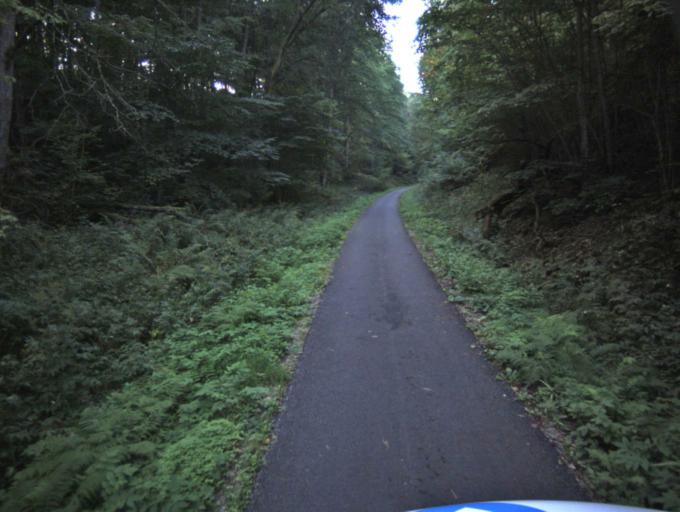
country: SE
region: Vaestra Goetaland
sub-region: Ulricehamns Kommun
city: Ulricehamn
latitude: 57.7290
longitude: 13.4096
